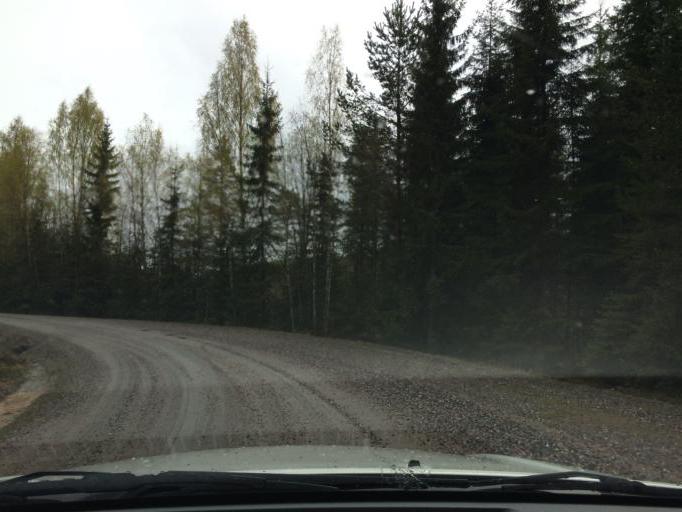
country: SE
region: OErebro
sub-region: Hallefors Kommun
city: Haellefors
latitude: 60.0163
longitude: 14.5868
